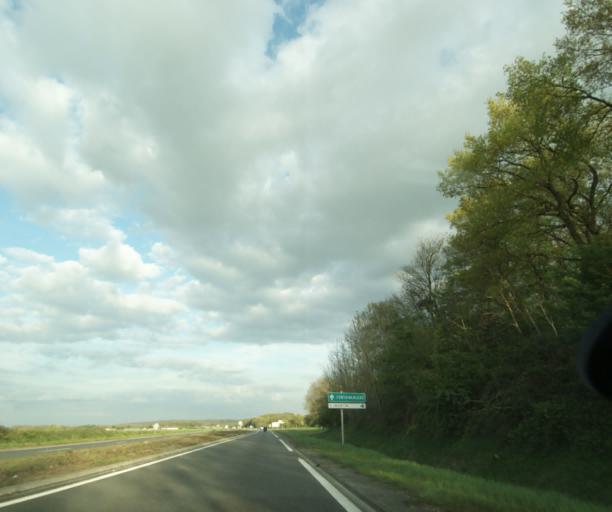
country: FR
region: Ile-de-France
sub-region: Departement de Seine-et-Marne
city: Barbizon
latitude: 48.4578
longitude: 2.5859
